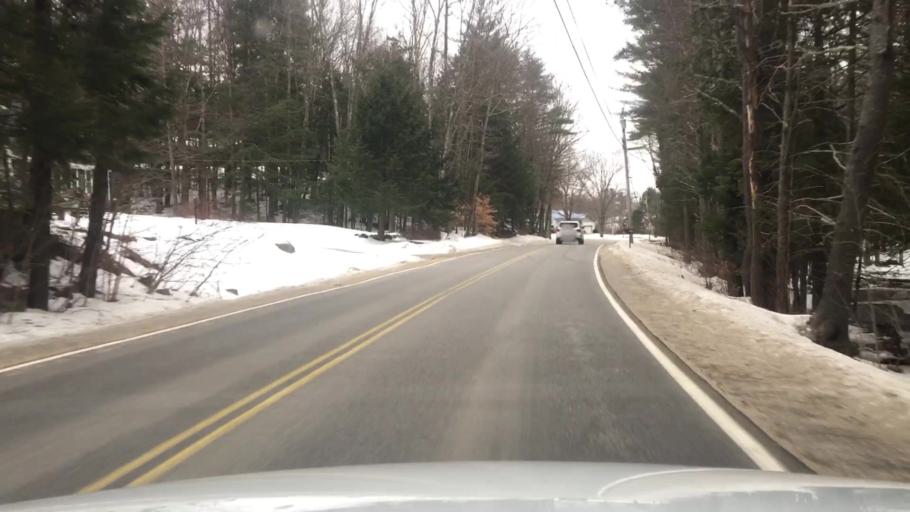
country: US
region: Maine
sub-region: York County
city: Springvale
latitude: 43.5044
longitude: -70.8149
